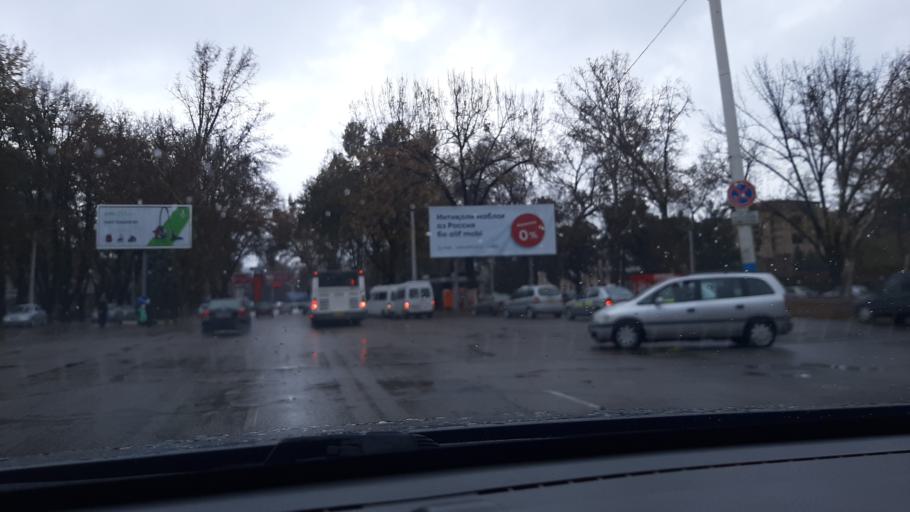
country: TJ
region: Viloyati Sughd
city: Khujand
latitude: 40.2853
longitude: 69.6226
